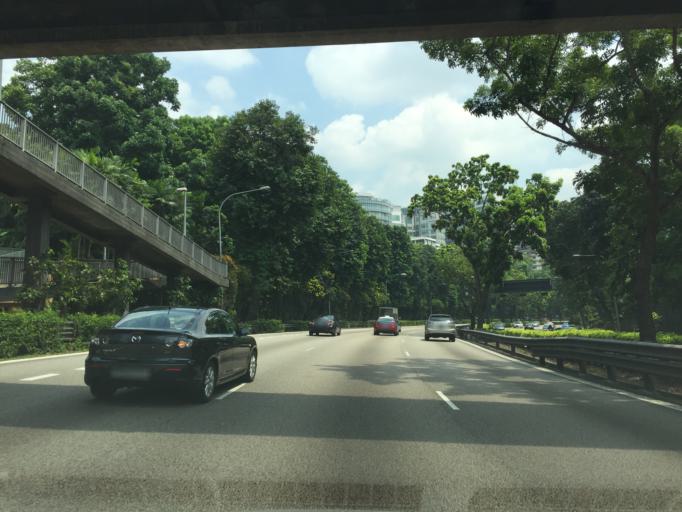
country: SG
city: Singapore
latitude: 1.3032
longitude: 103.8407
